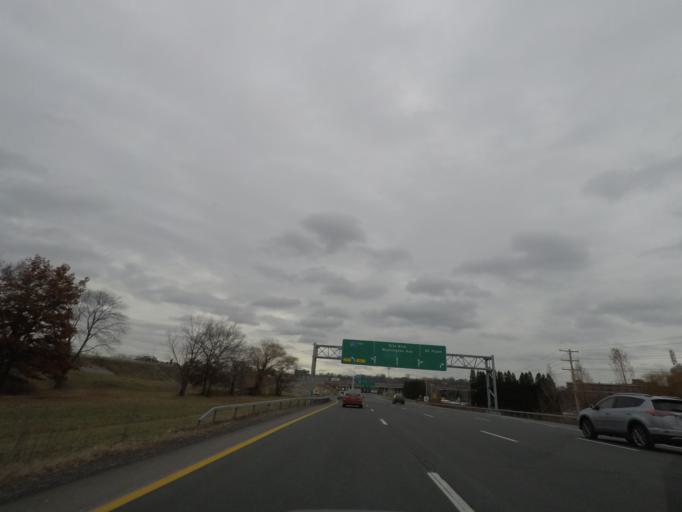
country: US
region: New York
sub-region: Schenectady County
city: Schenectady
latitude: 42.8129
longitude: -73.9554
